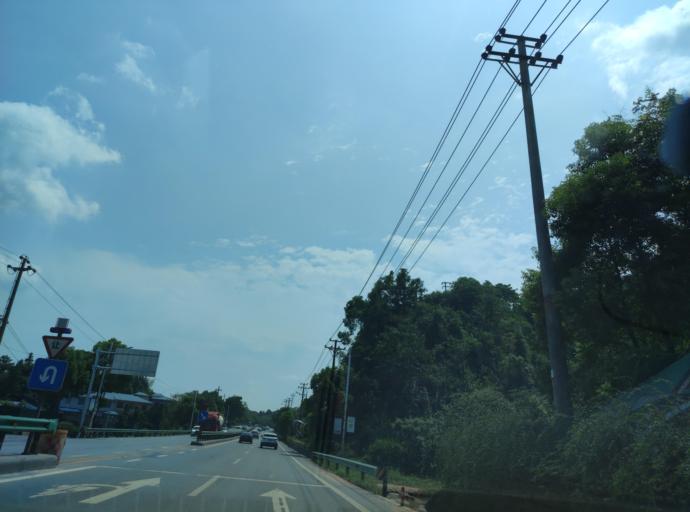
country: CN
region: Jiangxi Sheng
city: Pingxiang
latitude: 27.6507
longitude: 113.9286
